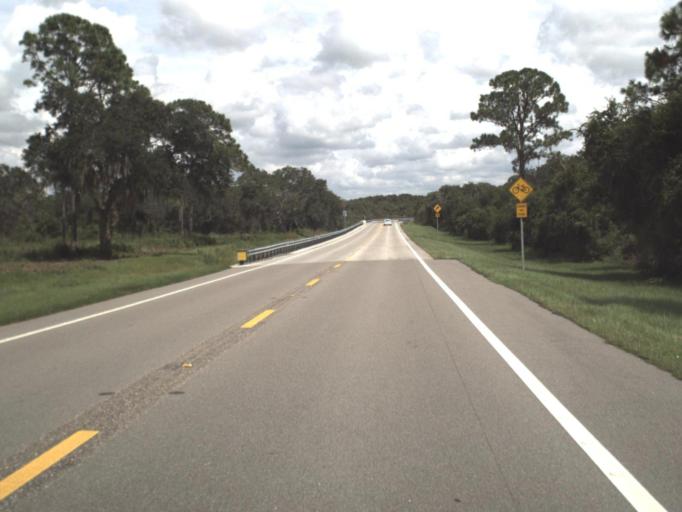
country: US
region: Florida
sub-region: Sarasota County
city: Lake Sarasota
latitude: 27.2424
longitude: -82.3258
